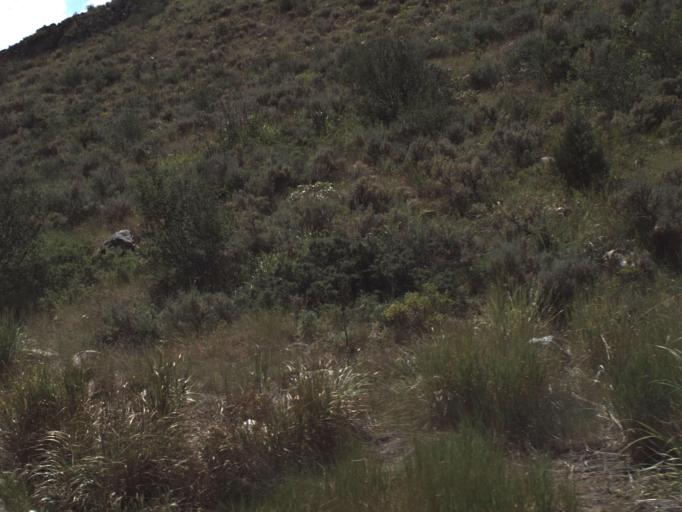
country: US
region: Utah
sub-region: Weber County
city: Wolf Creek
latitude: 41.3513
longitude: -111.5953
